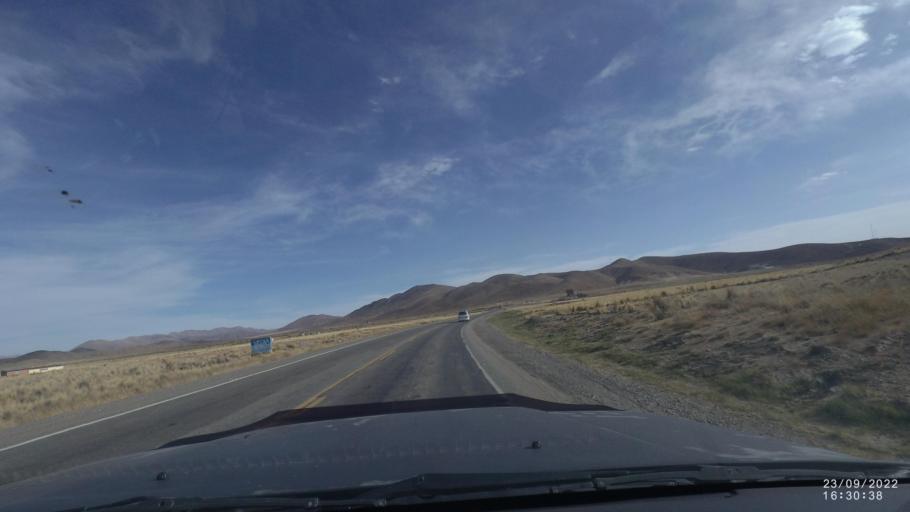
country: BO
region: Oruro
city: Machacamarca
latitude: -18.1566
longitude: -66.9862
